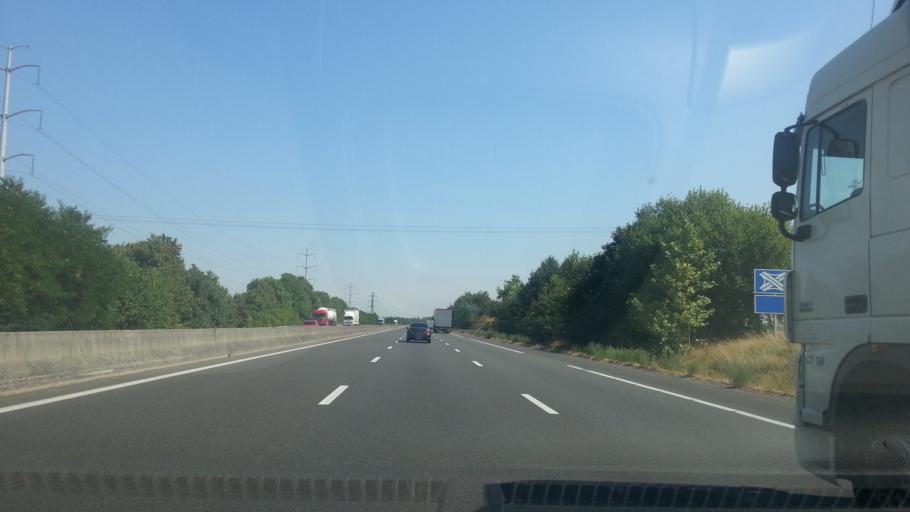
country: FR
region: Centre
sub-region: Departement du Loiret
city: Meung-sur-Loire
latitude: 47.8385
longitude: 1.6718
